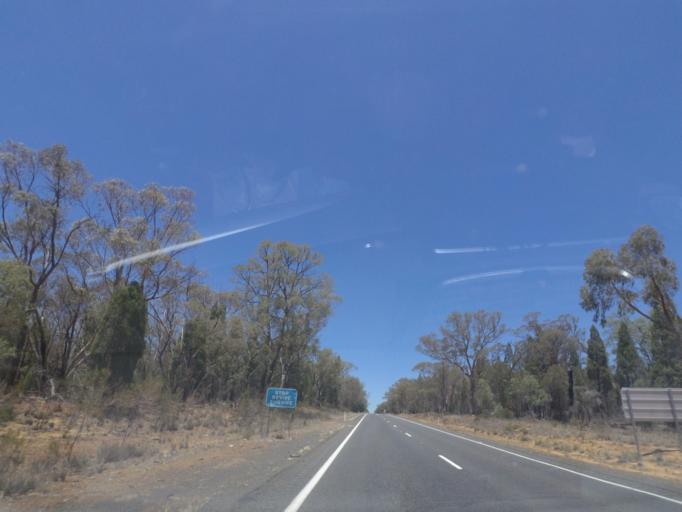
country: AU
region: New South Wales
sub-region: Warrumbungle Shire
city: Coonabarabran
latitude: -30.8511
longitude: 149.4581
